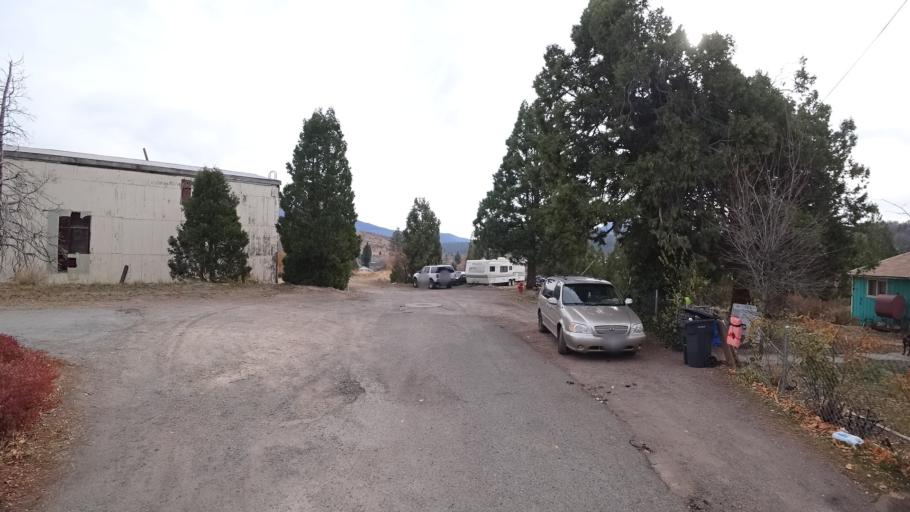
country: US
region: California
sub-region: Siskiyou County
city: Weed
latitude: 41.4271
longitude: -122.3878
